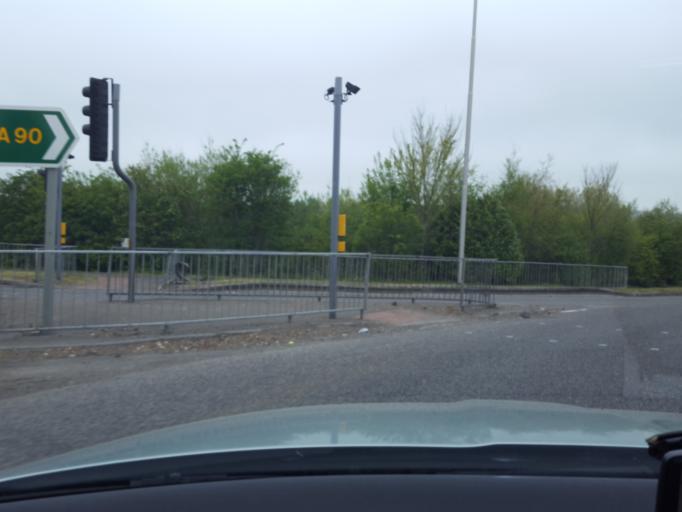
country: GB
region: Scotland
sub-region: Dundee City
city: Dundee
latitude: 56.4803
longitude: -2.9529
